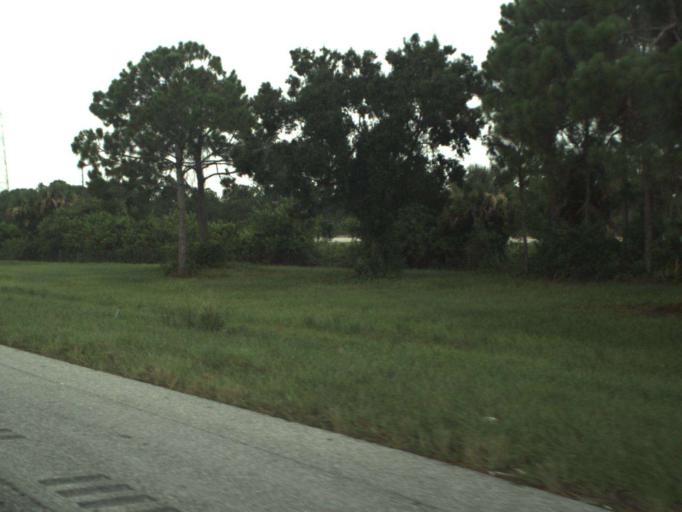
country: US
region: Florida
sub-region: Martin County
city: Port Salerno
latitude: 27.0913
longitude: -80.2546
